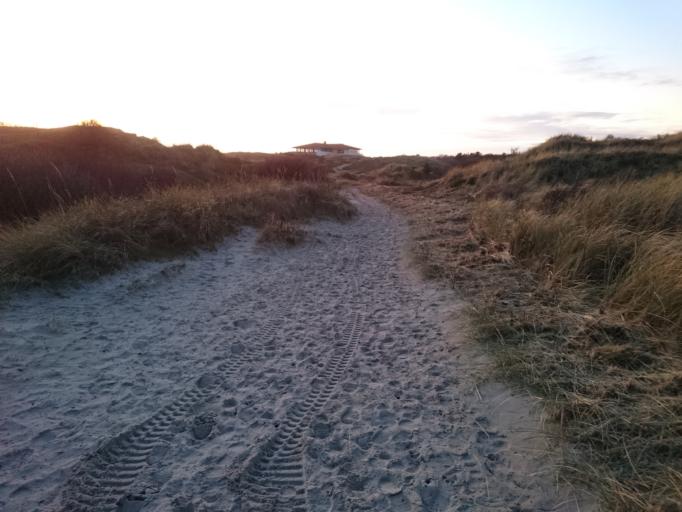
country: DK
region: North Denmark
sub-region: Frederikshavn Kommune
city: Skagen
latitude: 57.7400
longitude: 10.6376
